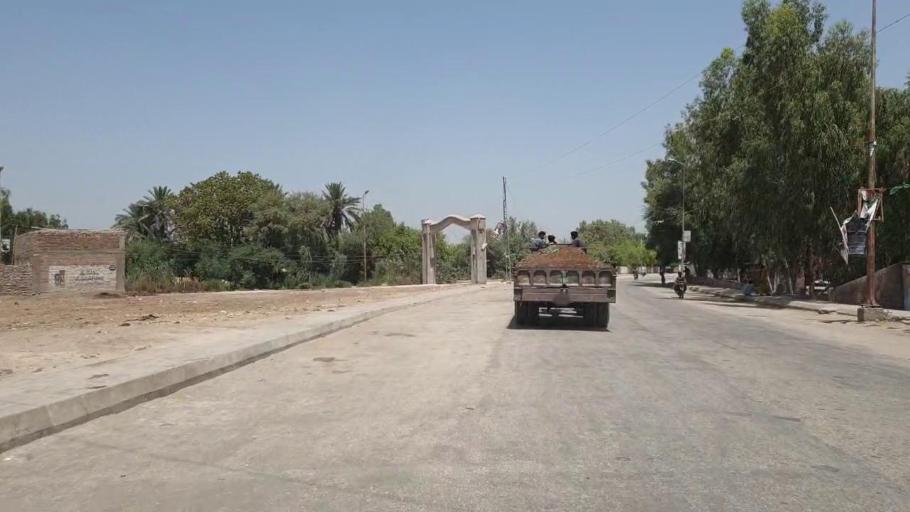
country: PK
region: Sindh
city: Adilpur
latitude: 27.9396
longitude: 69.3187
